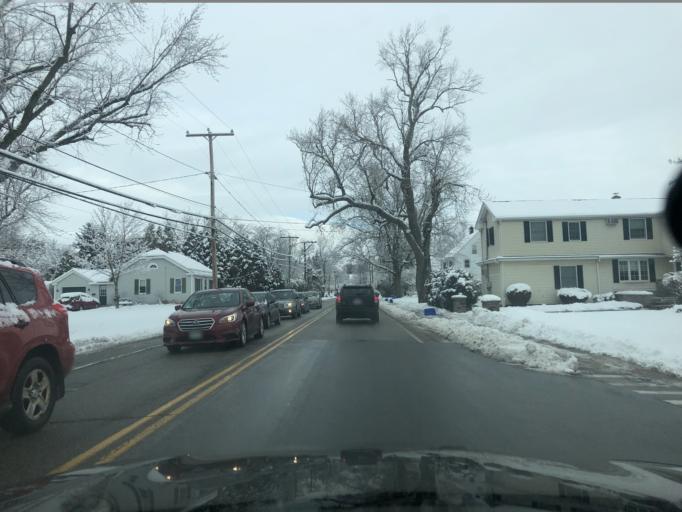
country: US
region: New Hampshire
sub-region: Strafford County
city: Somersworth
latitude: 43.2484
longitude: -70.8735
